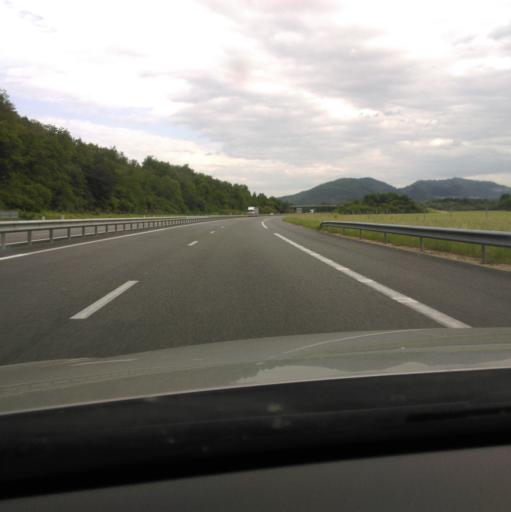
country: FR
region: Rhone-Alpes
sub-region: Departement de l'Ain
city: Saint-Martin-du-Frene
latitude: 46.1526
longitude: 5.5468
